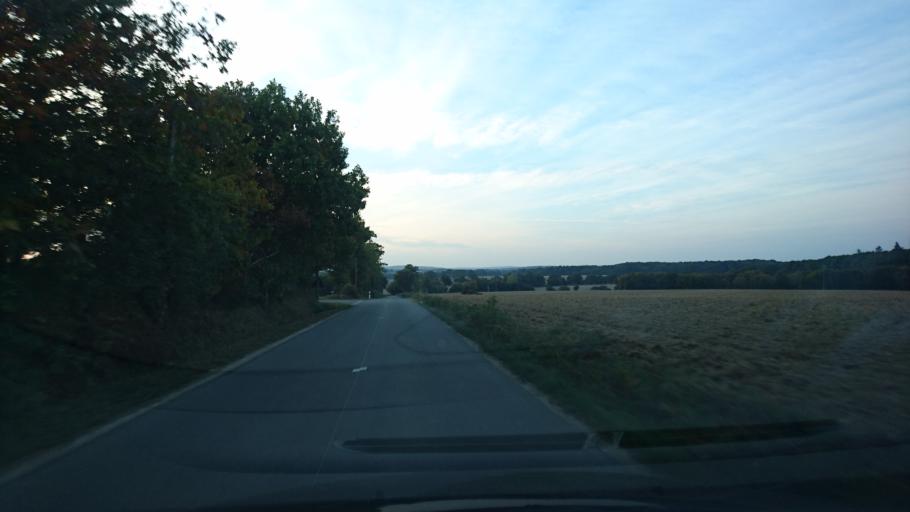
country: FR
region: Brittany
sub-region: Departement d'Ille-et-Vilaine
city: Maure-de-Bretagne
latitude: 47.8635
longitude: -2.0334
